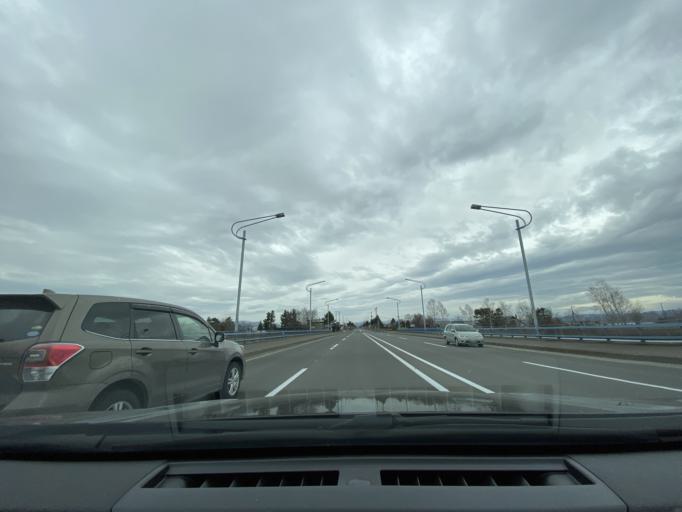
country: JP
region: Hokkaido
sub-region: Asahikawa-shi
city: Asahikawa
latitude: 43.8214
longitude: 142.4512
